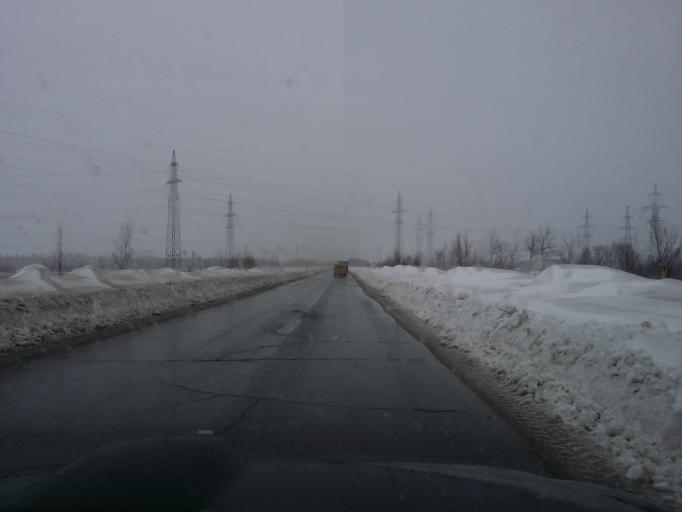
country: RU
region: Khanty-Mansiyskiy Avtonomnyy Okrug
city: Izluchinsk
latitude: 60.9721
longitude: 76.8923
